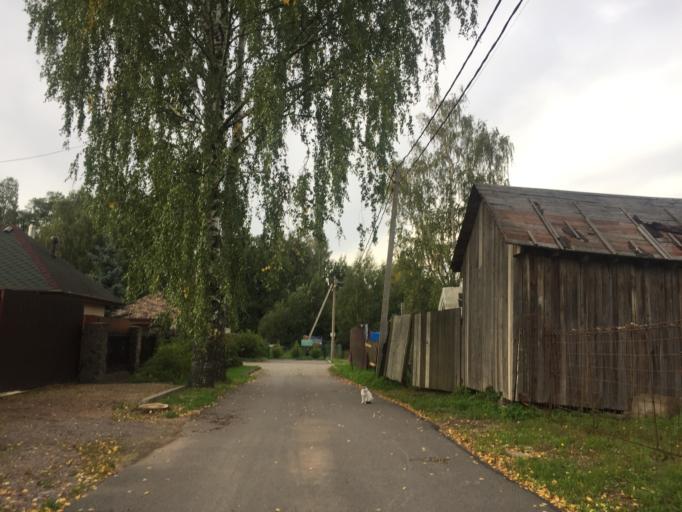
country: RU
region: Leningrad
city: Murino
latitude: 60.0487
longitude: 30.4571
